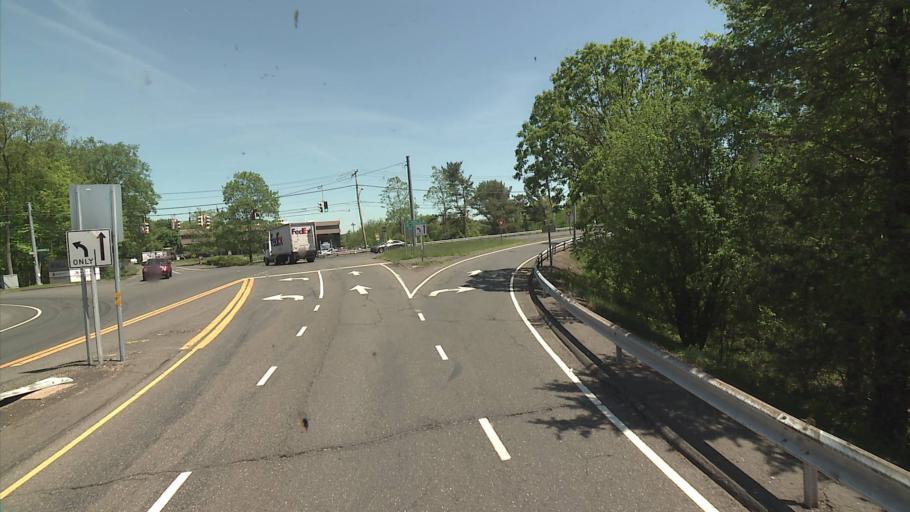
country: US
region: Connecticut
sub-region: Hartford County
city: Farmington
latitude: 41.7069
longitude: -72.8042
